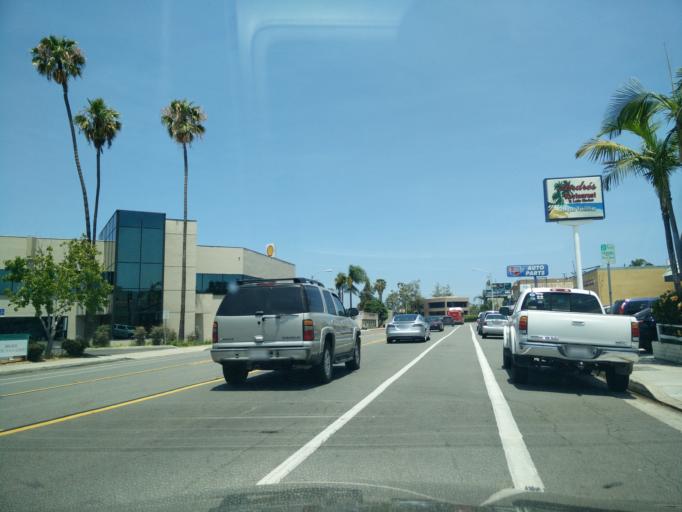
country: US
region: California
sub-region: San Diego County
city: San Diego
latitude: 32.7704
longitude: -117.2016
